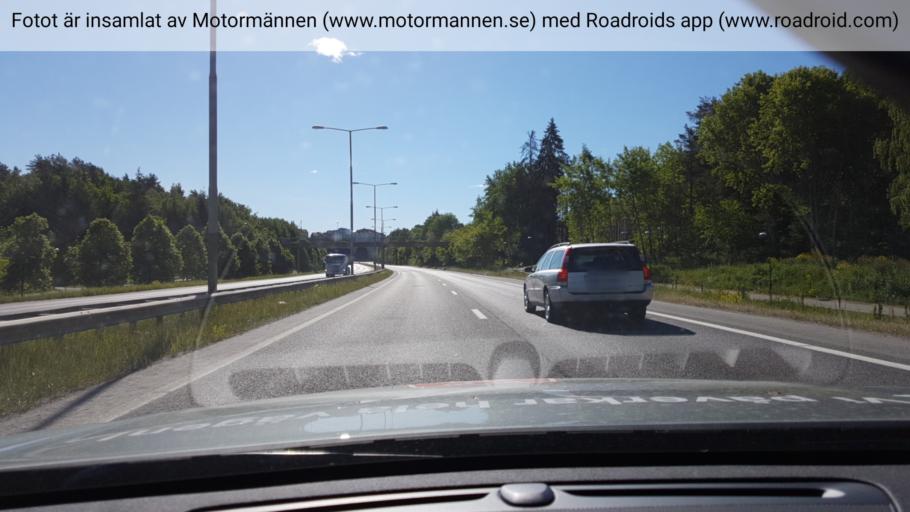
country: SE
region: Stockholm
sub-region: Stockholms Kommun
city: Arsta
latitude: 59.2606
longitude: 18.0705
